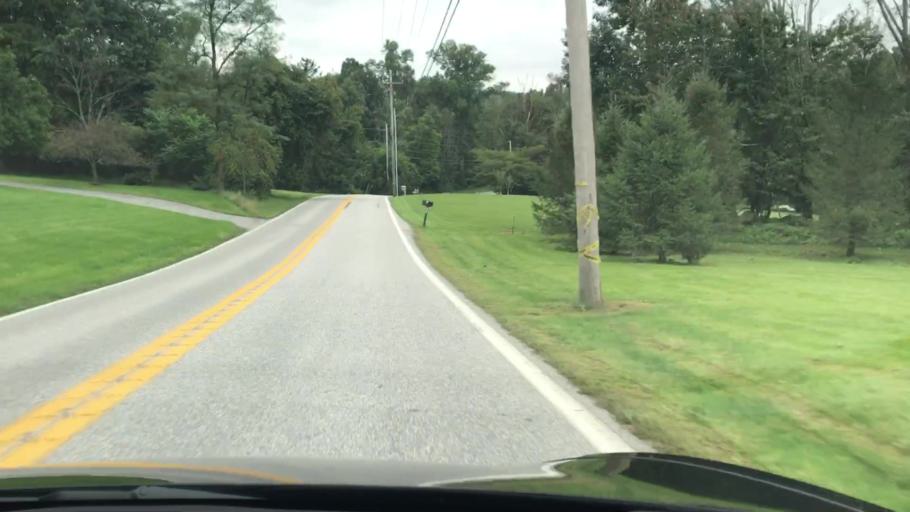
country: US
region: Pennsylvania
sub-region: York County
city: Dillsburg
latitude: 40.1348
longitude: -76.9620
